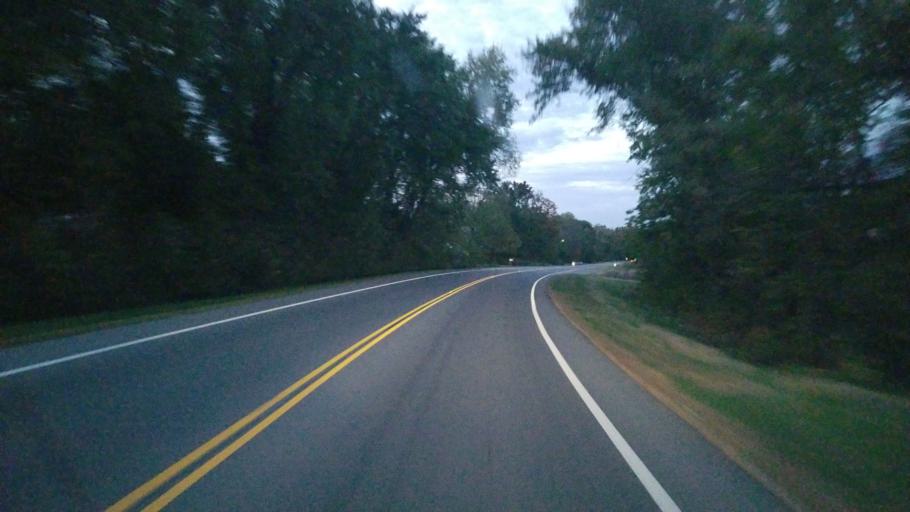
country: US
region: Ohio
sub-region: Scioto County
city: West Portsmouth
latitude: 38.7889
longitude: -83.0140
